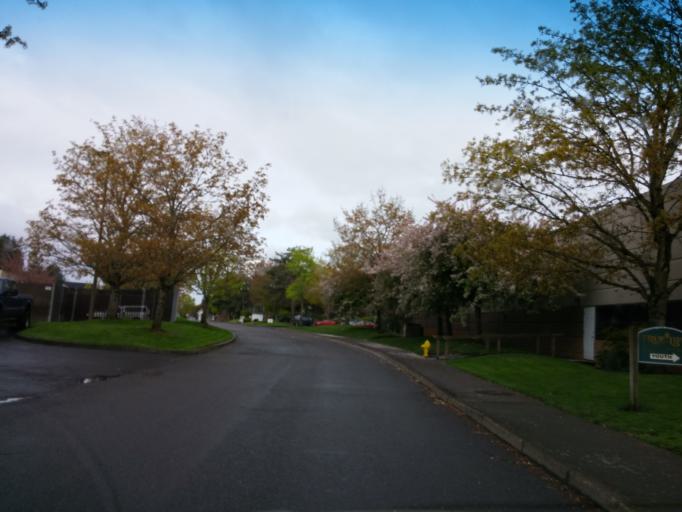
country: US
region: Oregon
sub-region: Washington County
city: Oak Hills
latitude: 45.5336
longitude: -122.8528
